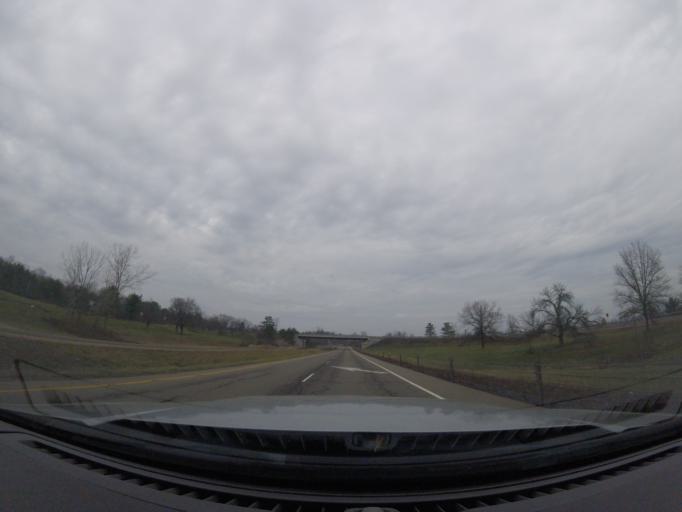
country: US
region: New York
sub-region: Schuyler County
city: Watkins Glen
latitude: 42.4202
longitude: -76.9032
